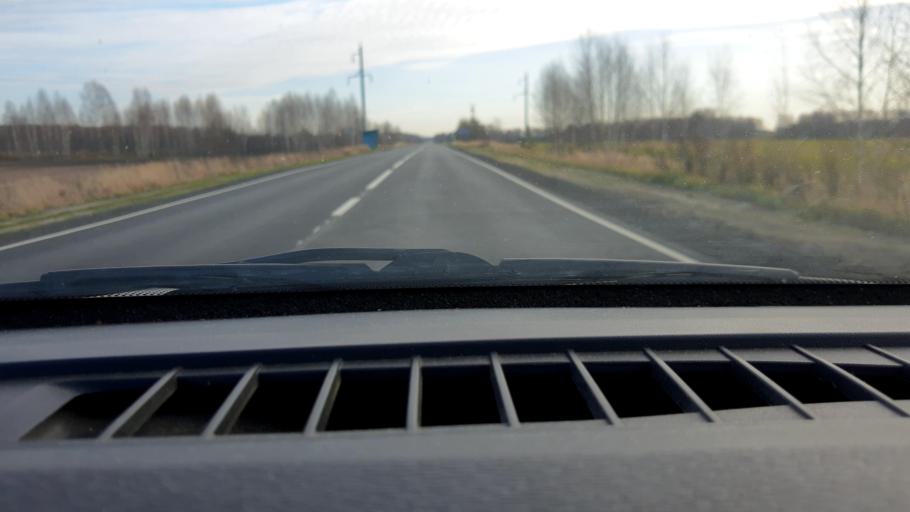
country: RU
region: Nizjnij Novgorod
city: Novaya Balakhna
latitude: 56.5885
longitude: 43.6674
